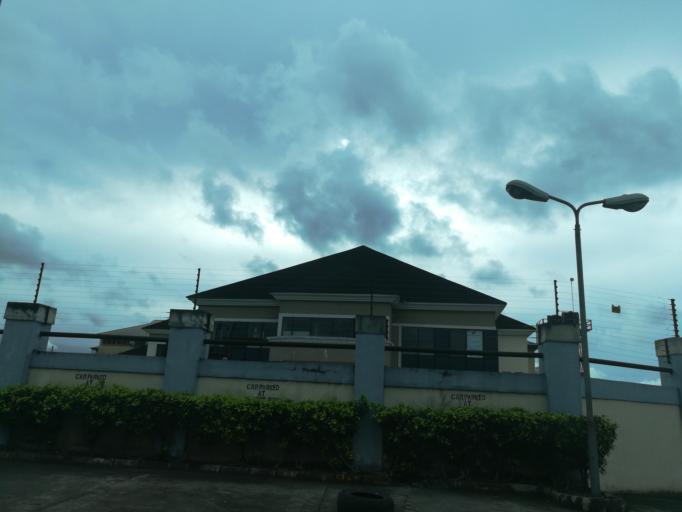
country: NG
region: Rivers
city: Port Harcourt
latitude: 4.8187
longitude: 6.9870
